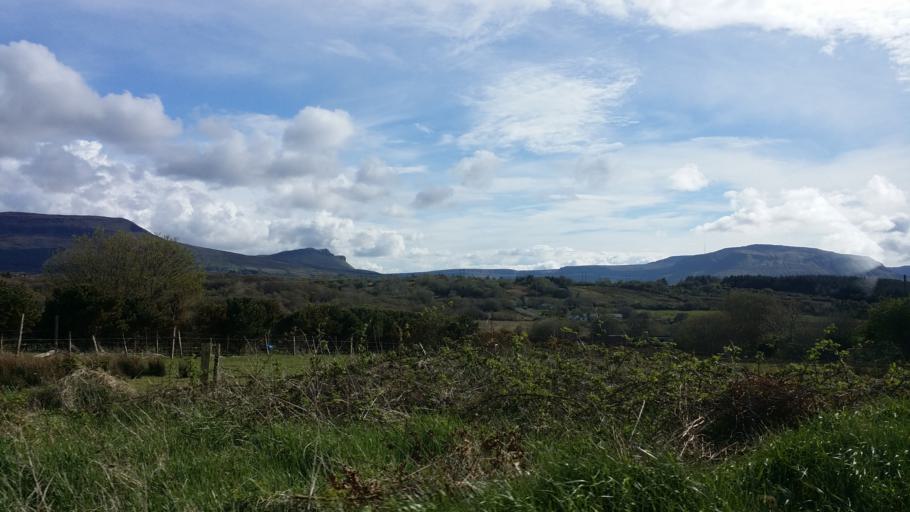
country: IE
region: Ulster
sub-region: County Donegal
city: Bundoran
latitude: 54.4670
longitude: -8.2797
